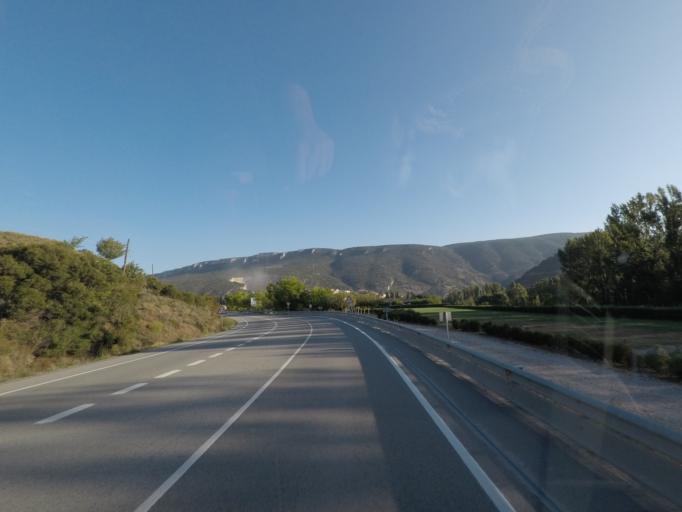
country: ES
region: Navarre
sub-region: Provincia de Navarra
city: Liedena
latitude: 42.6112
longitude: -1.2774
